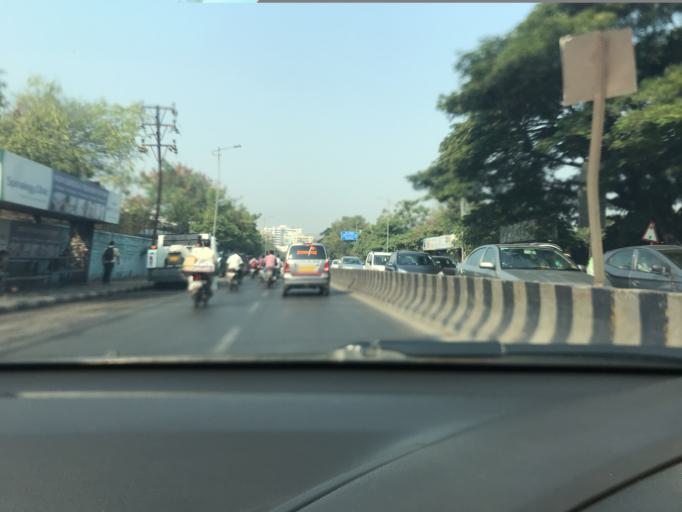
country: IN
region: Maharashtra
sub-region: Pune Division
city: Khadki
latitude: 18.5500
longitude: 73.8095
